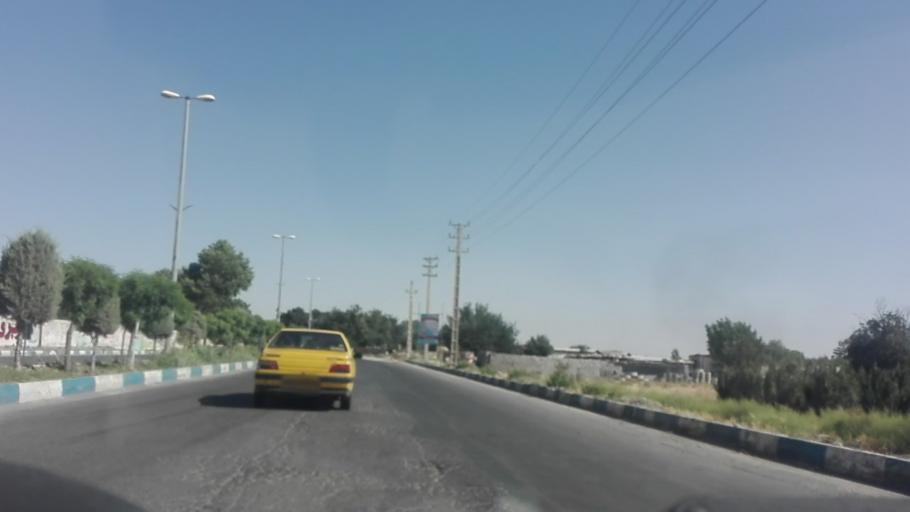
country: IR
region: Tehran
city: Shahriar
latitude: 35.6236
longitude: 51.0631
